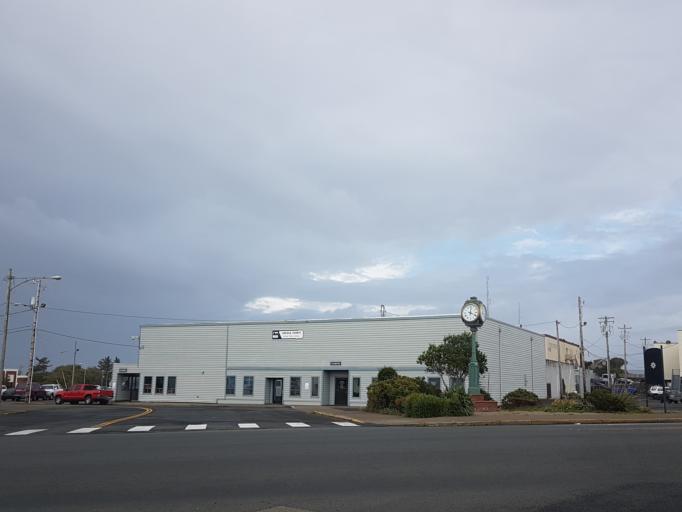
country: US
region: Oregon
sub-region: Lincoln County
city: Newport
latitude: 44.6344
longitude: -124.0542
